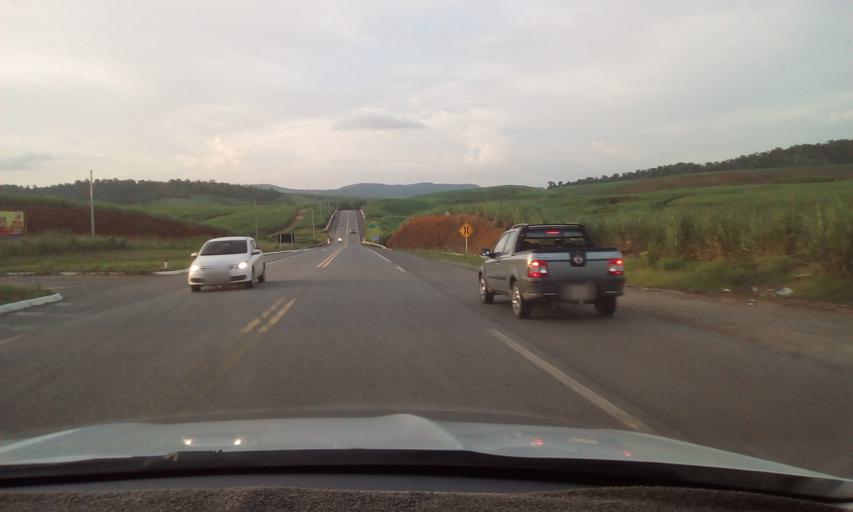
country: BR
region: Pernambuco
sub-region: Vicencia
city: Vicencia
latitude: -7.6537
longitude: -35.2506
